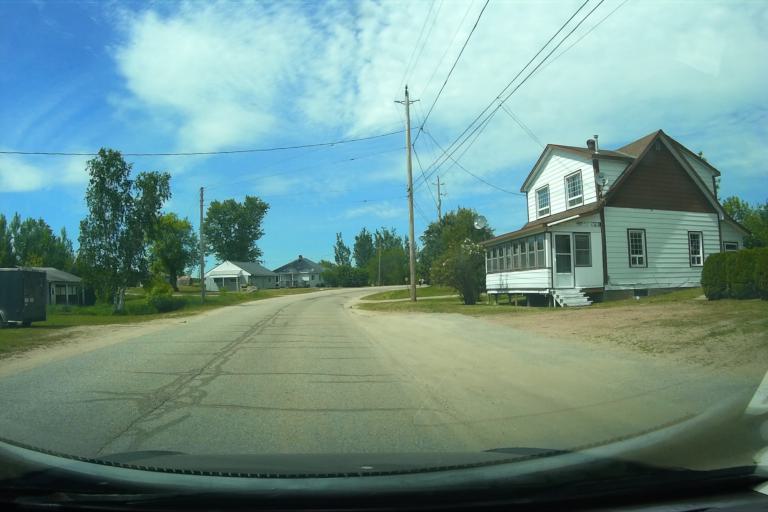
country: CA
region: Ontario
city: Powassan
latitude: 46.2326
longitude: -79.1477
